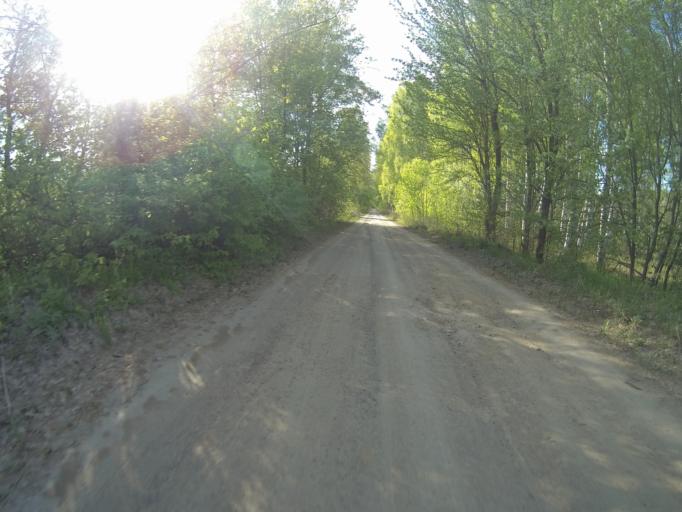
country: RU
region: Vladimir
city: Raduzhnyy
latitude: 56.0039
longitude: 40.2652
